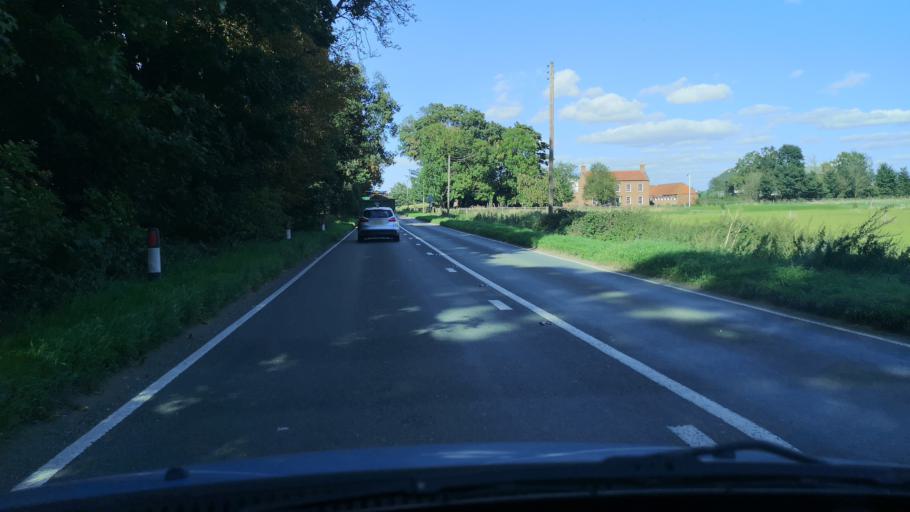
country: GB
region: England
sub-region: North Lincolnshire
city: Crowle
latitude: 53.5800
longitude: -0.8213
